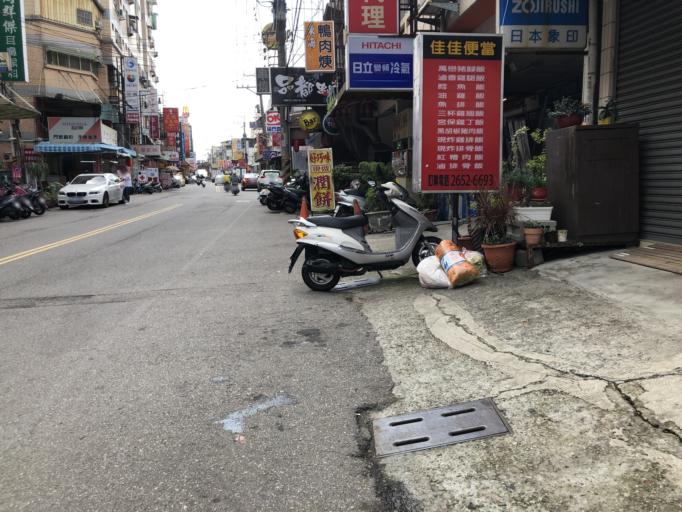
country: TW
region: Taiwan
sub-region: Taichung City
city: Taichung
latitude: 24.1814
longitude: 120.5866
